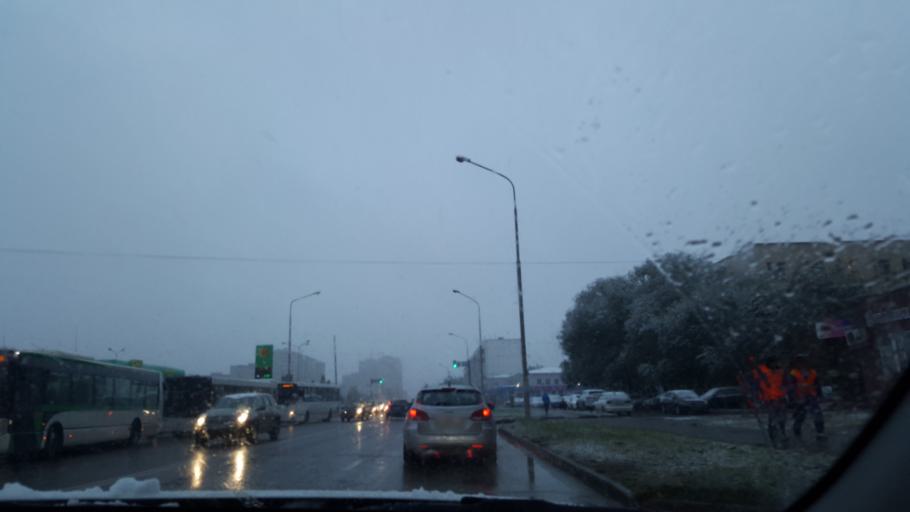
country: KZ
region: Astana Qalasy
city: Astana
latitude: 51.1570
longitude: 71.4974
